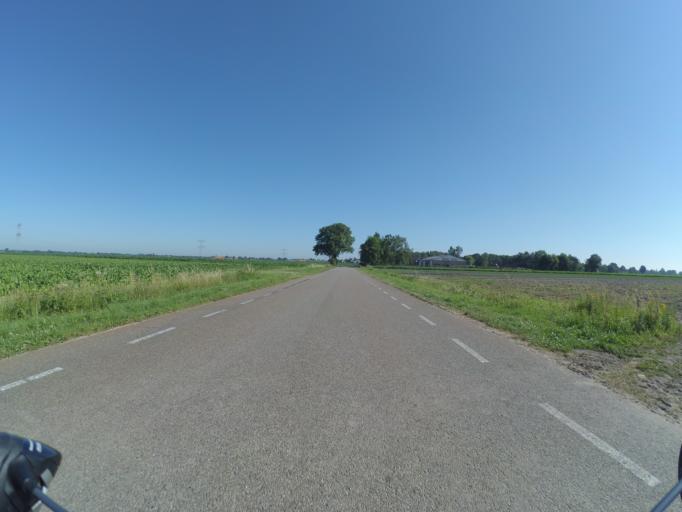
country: NL
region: North Brabant
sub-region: Gemeente Made en Drimmelen
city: Made
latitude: 51.6506
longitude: 4.8084
